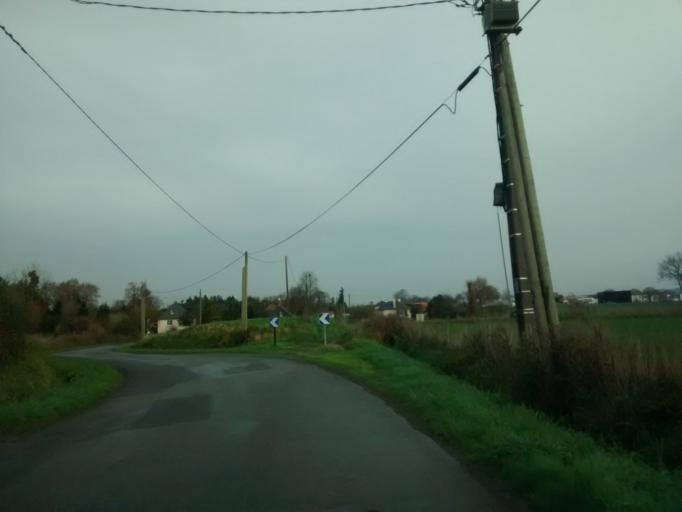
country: FR
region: Brittany
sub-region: Departement d'Ille-et-Vilaine
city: Noyal-sur-Vilaine
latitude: 48.1091
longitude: -1.5404
